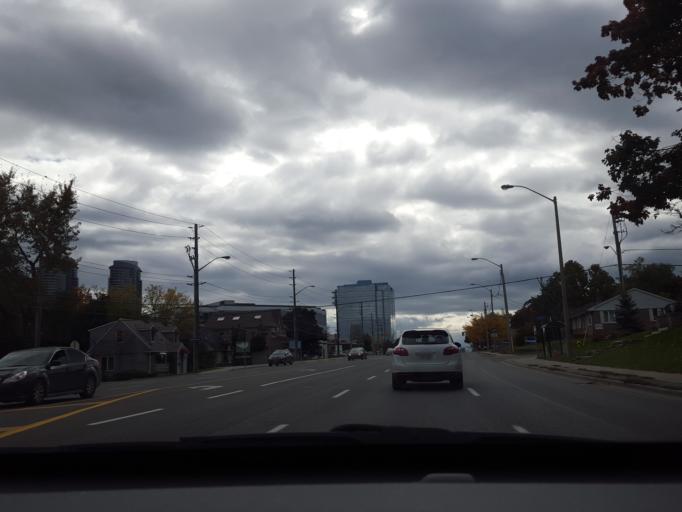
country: CA
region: Ontario
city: Scarborough
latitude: 43.7822
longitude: -79.2877
